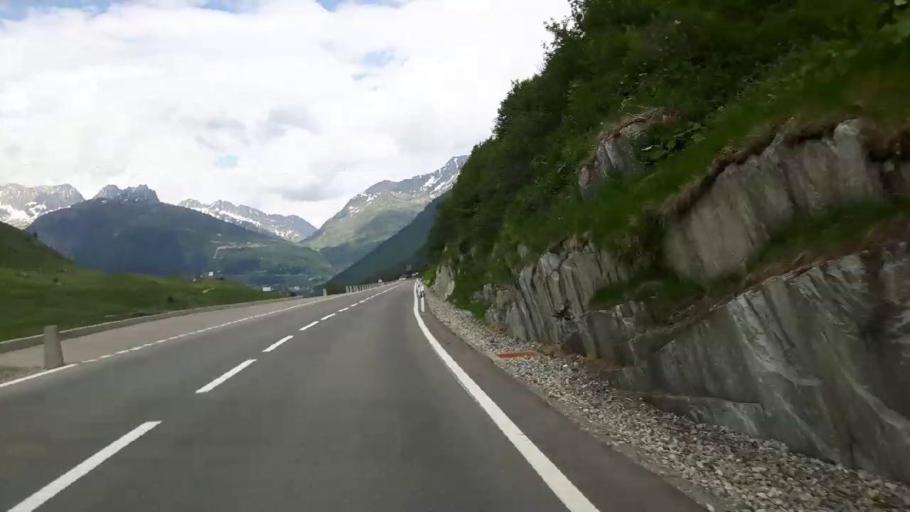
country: CH
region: Uri
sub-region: Uri
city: Andermatt
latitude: 46.6137
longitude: 8.5501
